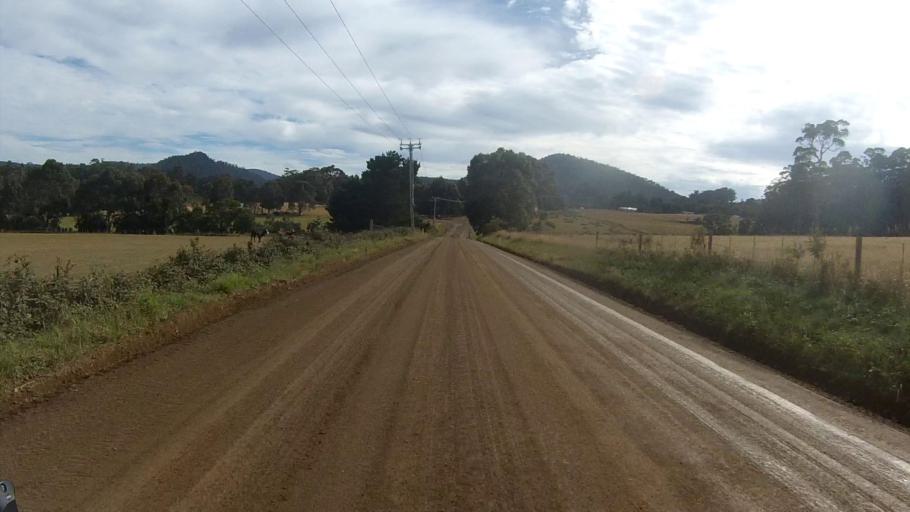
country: AU
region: Tasmania
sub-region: Sorell
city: Sorell
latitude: -42.7822
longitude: 147.8091
